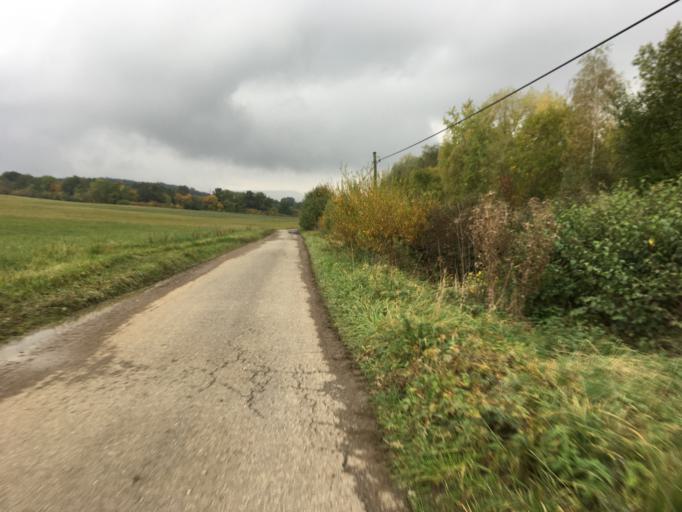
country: DE
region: Baden-Wuerttemberg
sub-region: Tuebingen Region
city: Nehren
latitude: 48.4330
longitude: 9.0804
